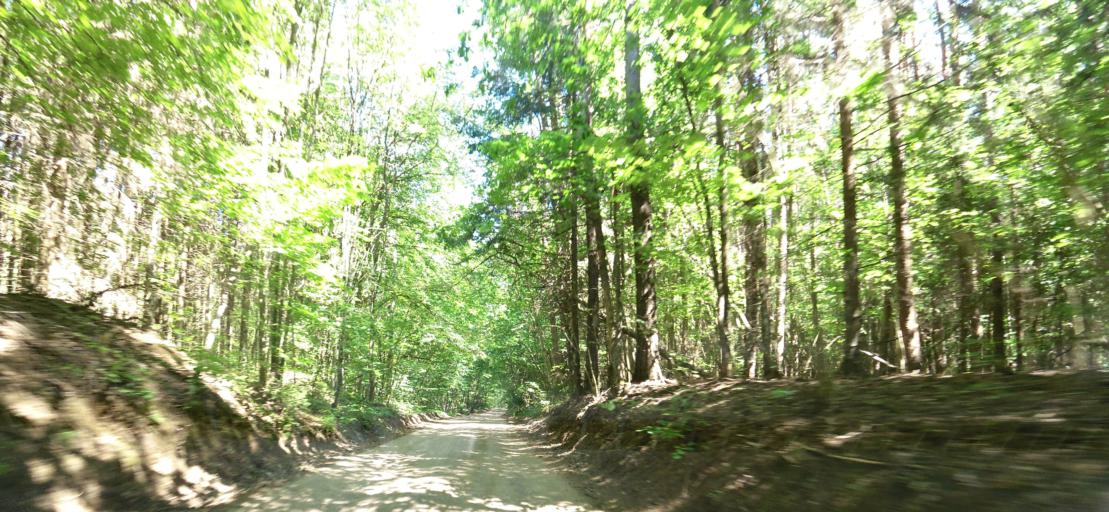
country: LT
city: Grigiskes
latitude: 54.8027
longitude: 24.9937
